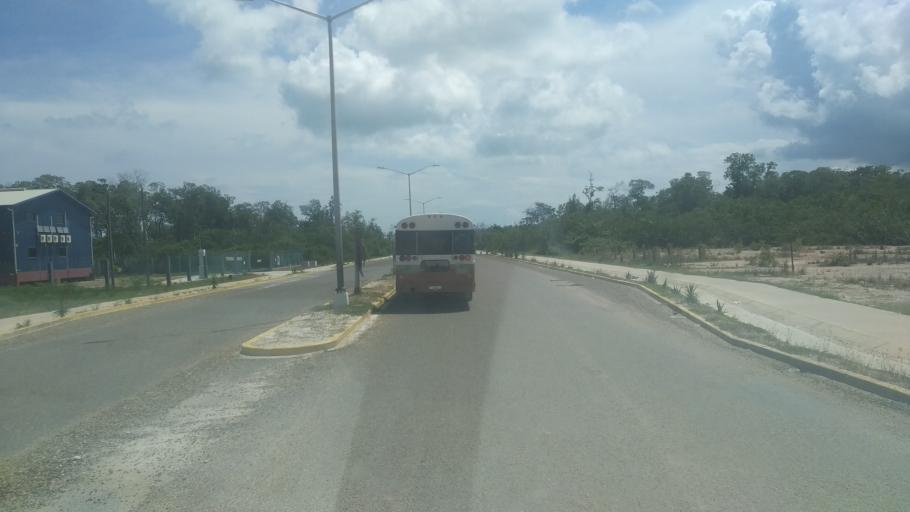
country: BZ
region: Belize
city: Belize City
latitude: 17.5034
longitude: -88.2221
